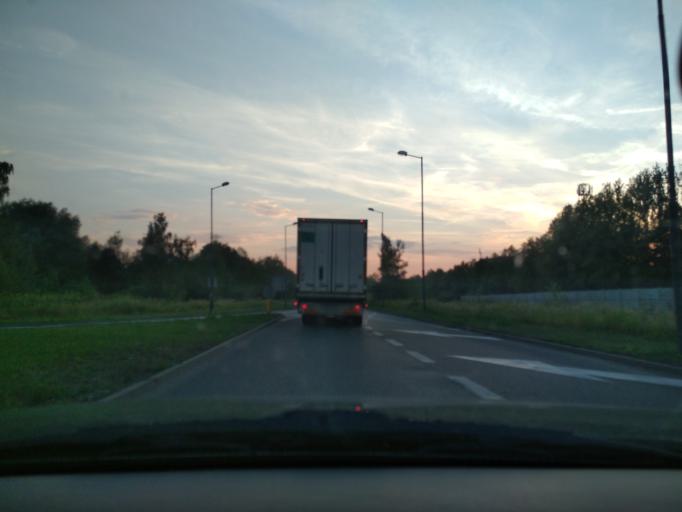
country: PL
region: Silesian Voivodeship
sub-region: Gliwice
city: Gliwice
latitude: 50.2713
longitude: 18.7018
